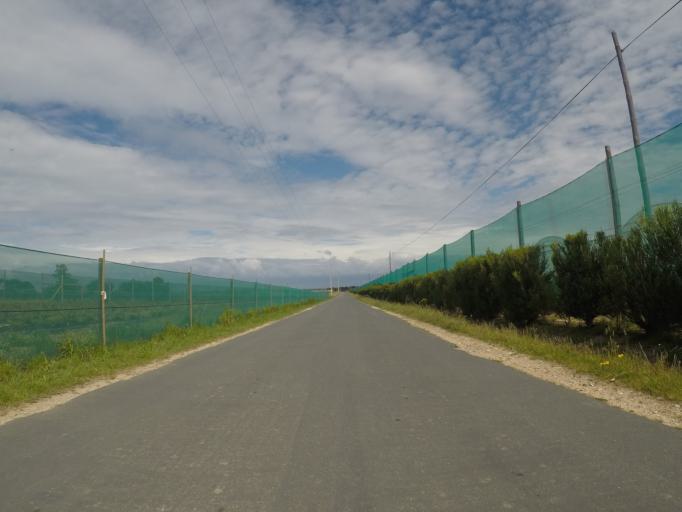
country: PT
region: Beja
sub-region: Odemira
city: Sao Teotonio
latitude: 37.4839
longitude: -8.7702
